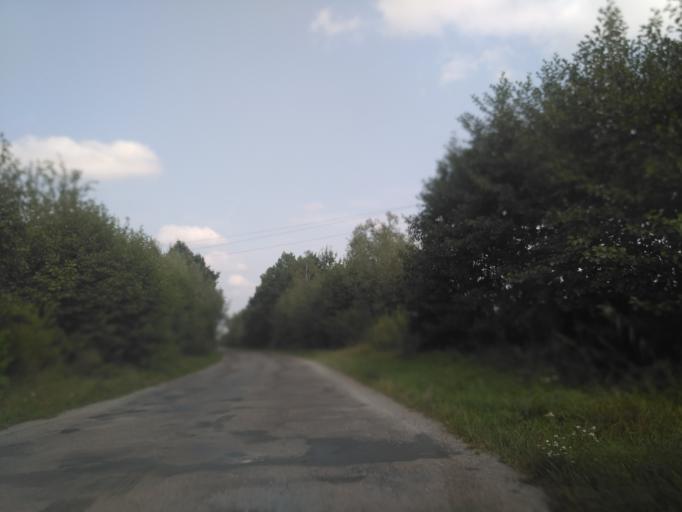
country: PL
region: Lublin Voivodeship
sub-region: Powiat wlodawski
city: Urszulin
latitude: 51.3760
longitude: 23.1662
